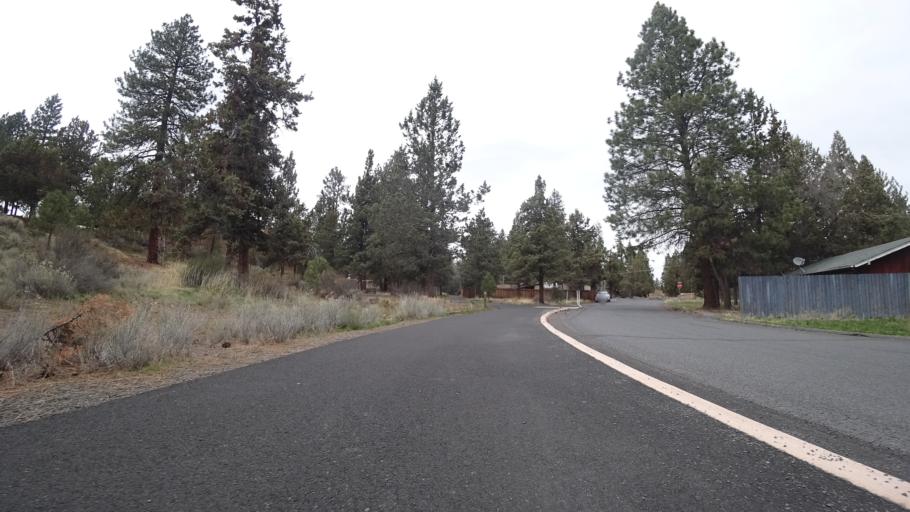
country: US
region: Oregon
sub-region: Deschutes County
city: Bend
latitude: 44.0520
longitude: -121.2910
